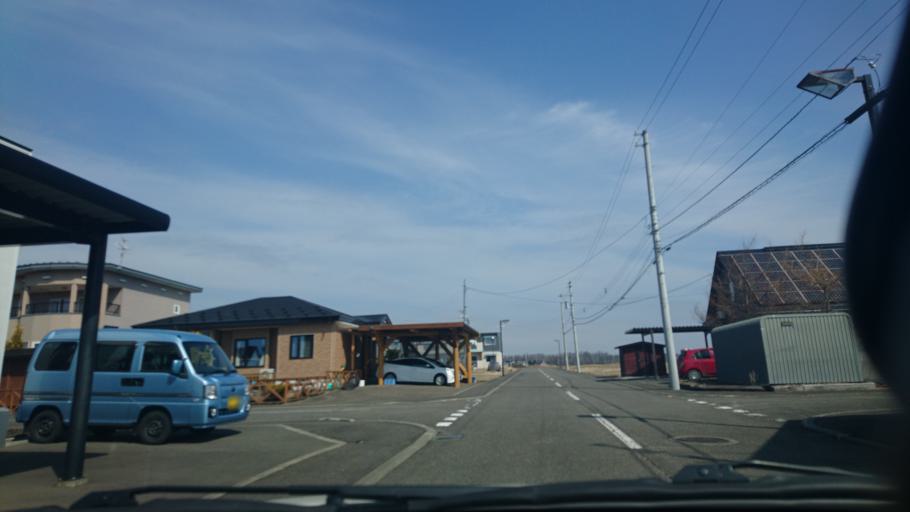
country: JP
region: Hokkaido
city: Otofuke
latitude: 43.0942
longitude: 143.2323
